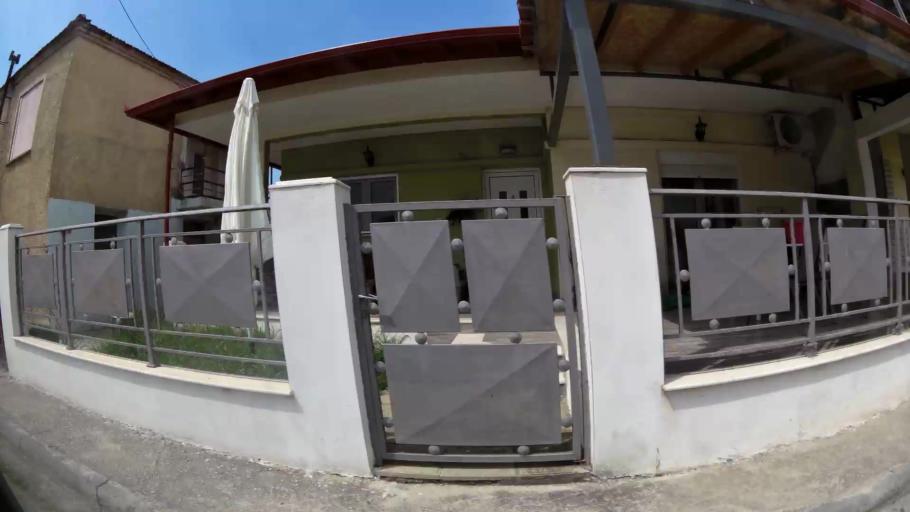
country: GR
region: Central Macedonia
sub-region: Nomos Pierias
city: Korinos
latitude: 40.3133
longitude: 22.5859
